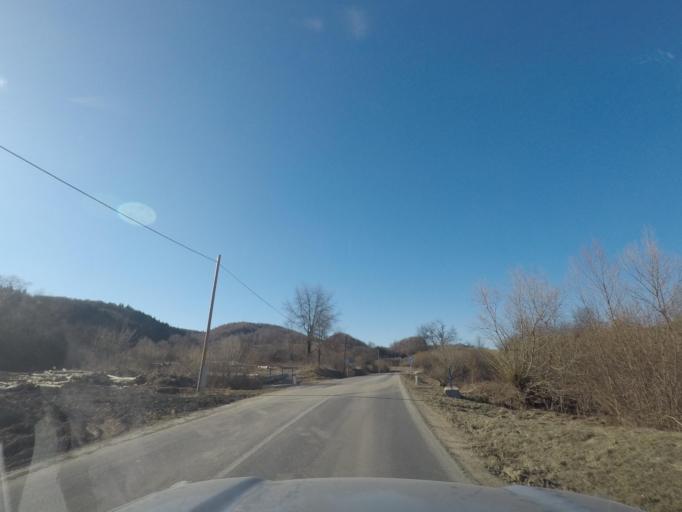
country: SK
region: Presovsky
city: Medzilaborce
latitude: 49.2003
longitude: 21.9936
